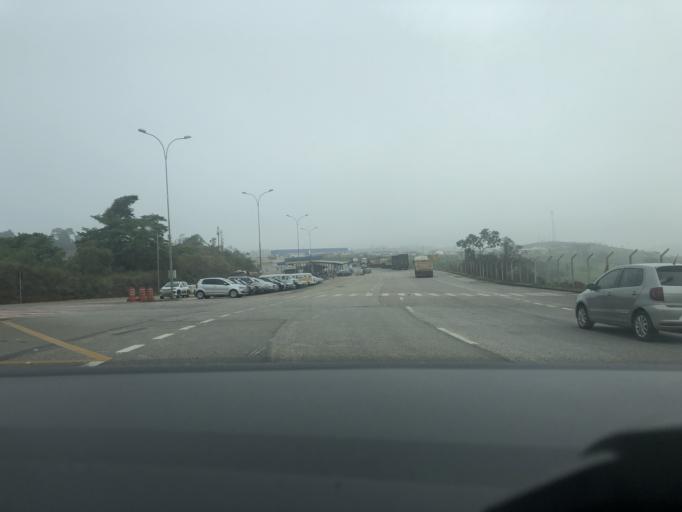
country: BR
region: Minas Gerais
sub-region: Congonhas
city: Congonhas
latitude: -20.5957
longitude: -43.9586
